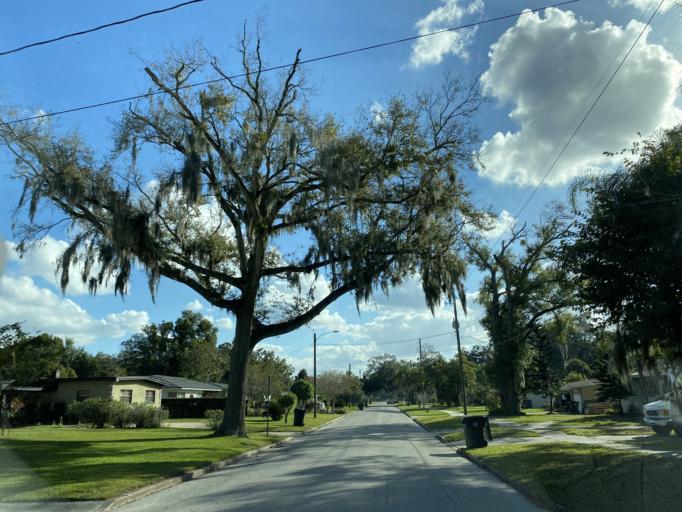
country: US
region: Florida
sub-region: Orange County
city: Orlando
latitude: 28.5515
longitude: -81.4046
